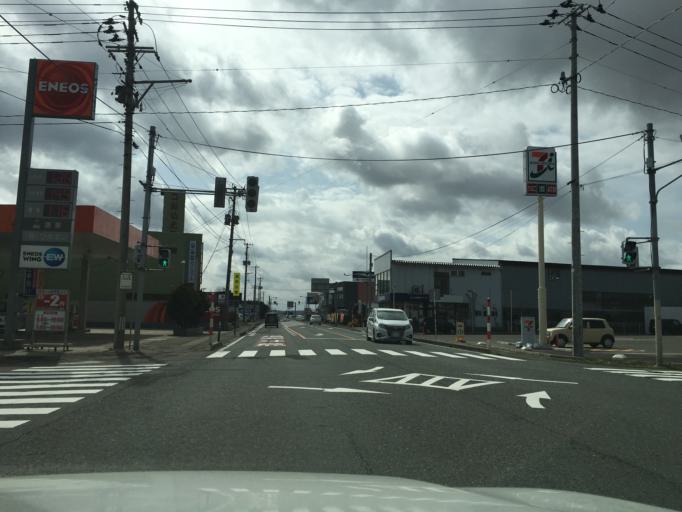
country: JP
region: Akita
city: Tenno
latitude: 39.9445
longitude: 140.0839
